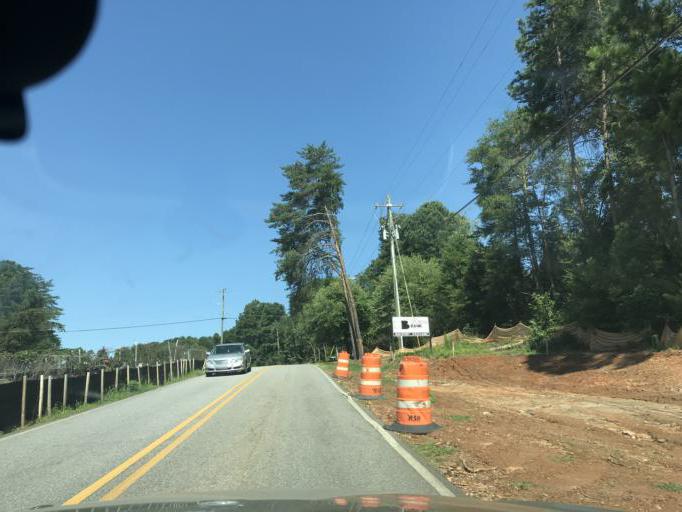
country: US
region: Georgia
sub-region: Forsyth County
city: Cumming
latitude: 34.2107
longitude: -84.1021
